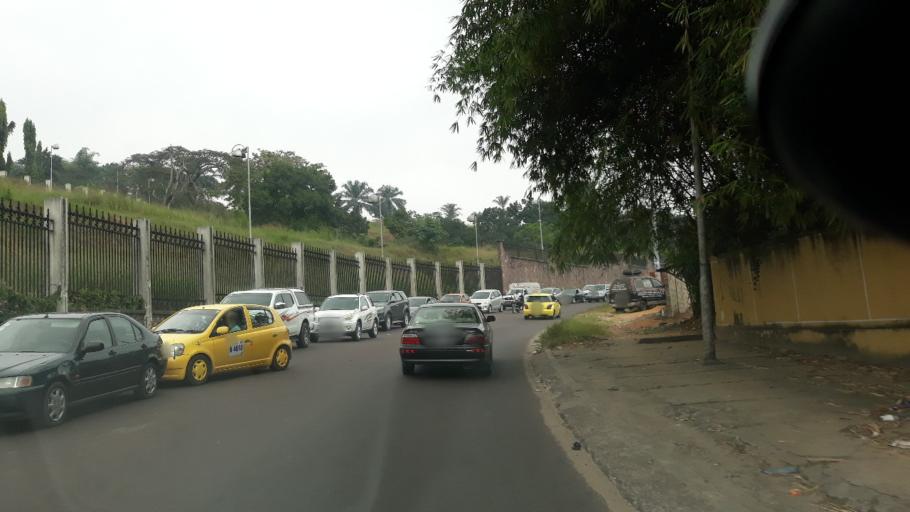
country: CD
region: Kinshasa
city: Kinshasa
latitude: -4.3617
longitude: 15.2526
